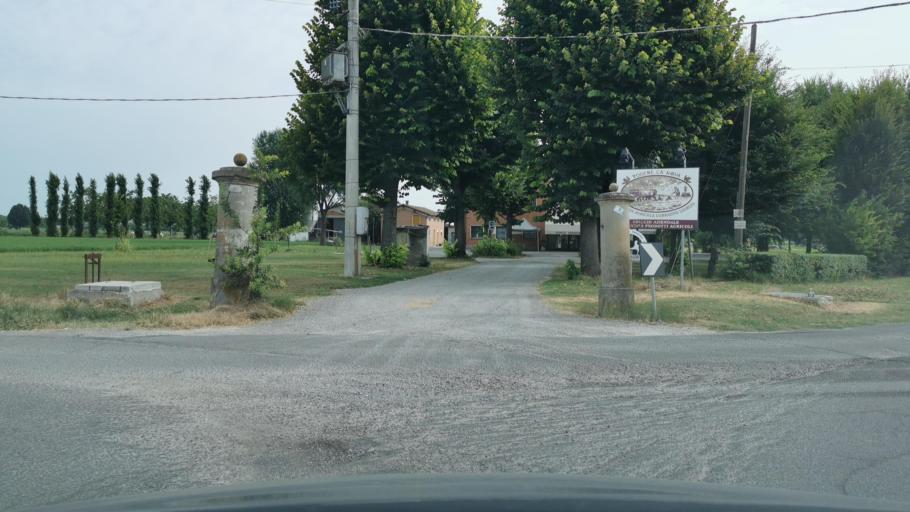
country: IT
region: Emilia-Romagna
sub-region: Provincia di Modena
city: Villanova
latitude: 44.6855
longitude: 10.9086
